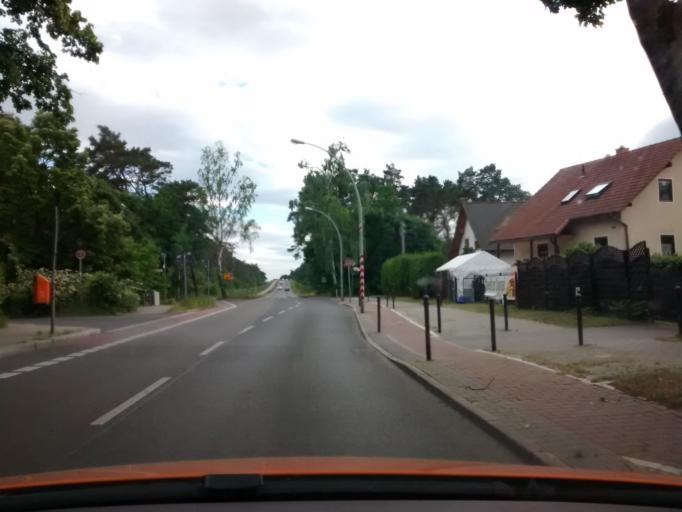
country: DE
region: Berlin
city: Bohnsdorf
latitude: 52.3899
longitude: 13.5710
